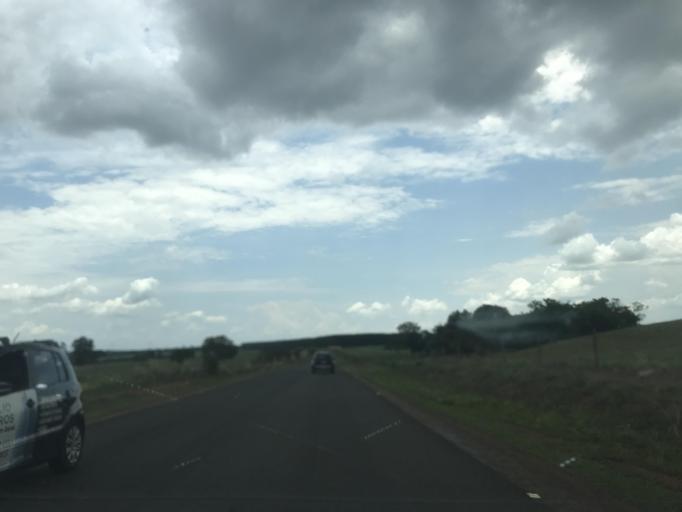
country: BR
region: Goias
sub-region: Vianopolis
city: Vianopolis
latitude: -16.9166
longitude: -48.5552
